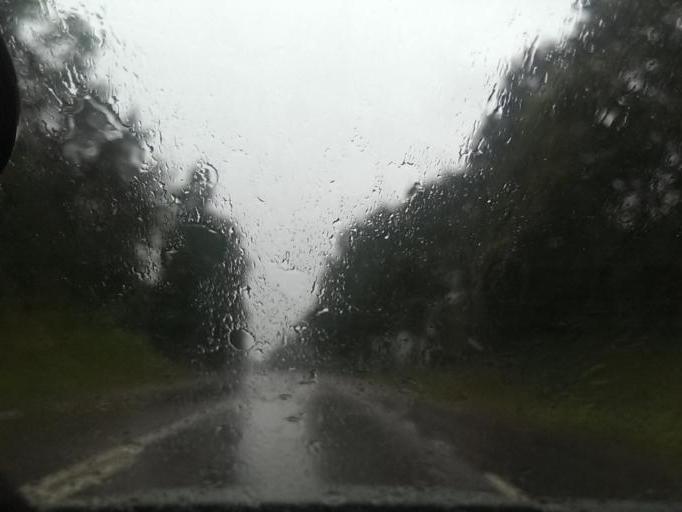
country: SE
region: Skane
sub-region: Orkelljunga Kommun
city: OErkelljunga
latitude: 56.2888
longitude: 13.2962
